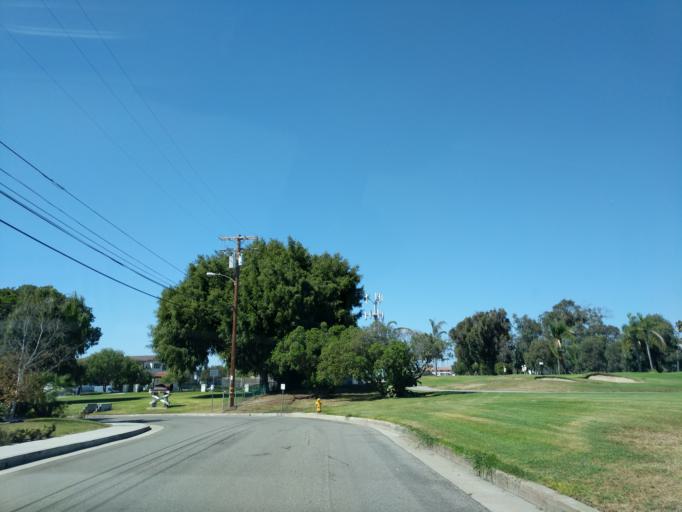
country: US
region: California
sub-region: Orange County
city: San Clemente
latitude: 33.4057
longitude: -117.5956
